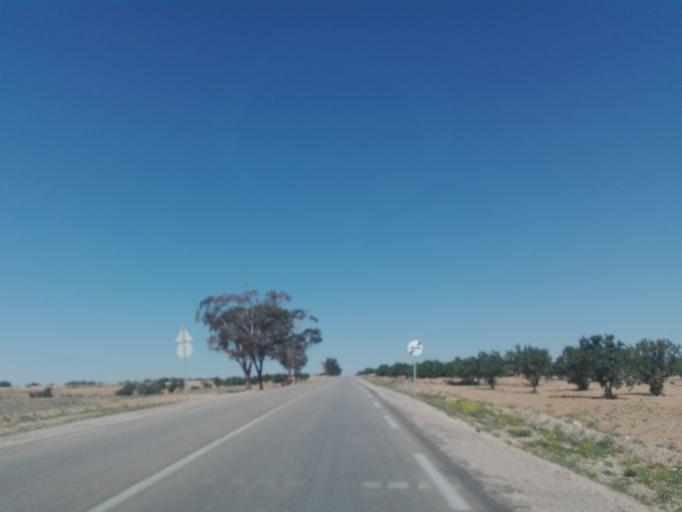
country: TN
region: Safaqis
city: Bi'r `Ali Bin Khalifah
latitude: 34.7475
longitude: 10.3541
